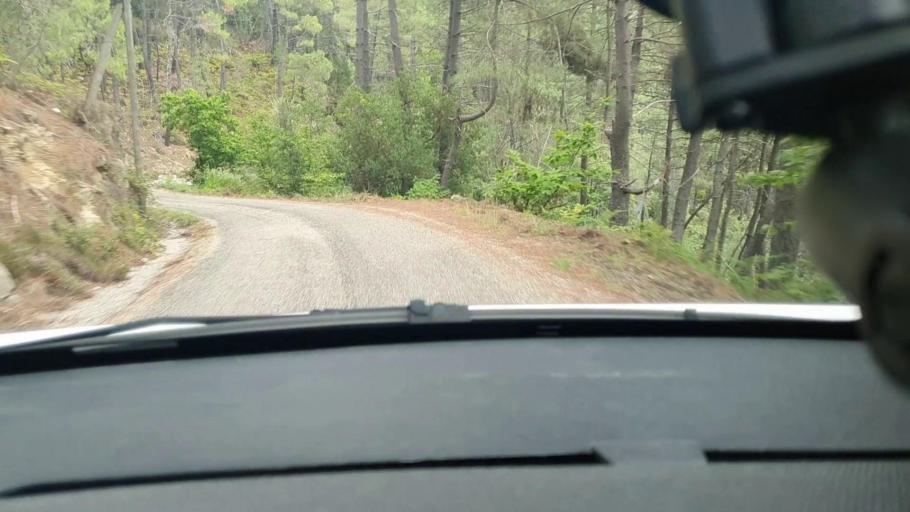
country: FR
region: Languedoc-Roussillon
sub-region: Departement du Gard
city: Branoux-les-Taillades
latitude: 44.2357
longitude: 3.9651
